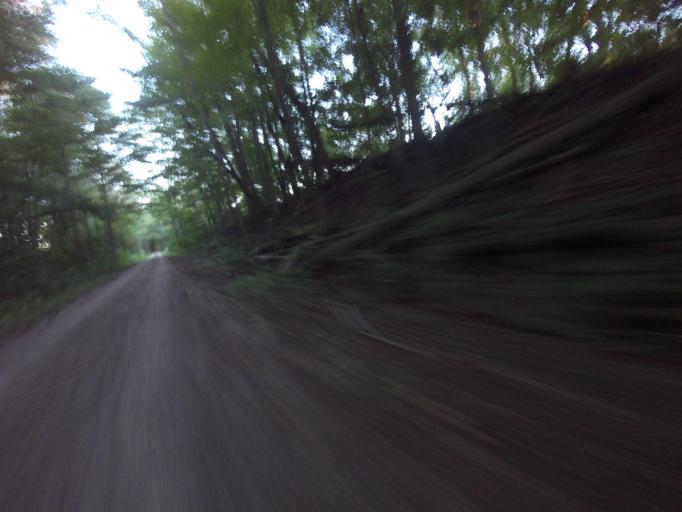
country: CA
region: Ontario
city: Goderich
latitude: 43.7478
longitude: -81.6451
